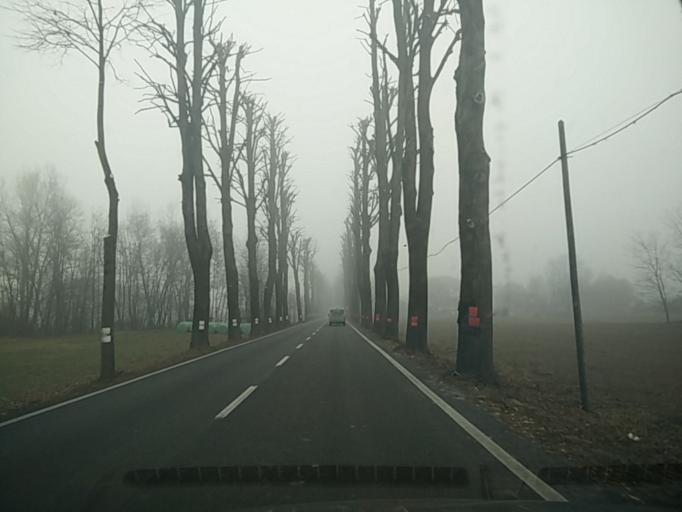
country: IT
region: Veneto
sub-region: Provincia di Belluno
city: Seren del Grappa
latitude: 46.0092
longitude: 11.8598
